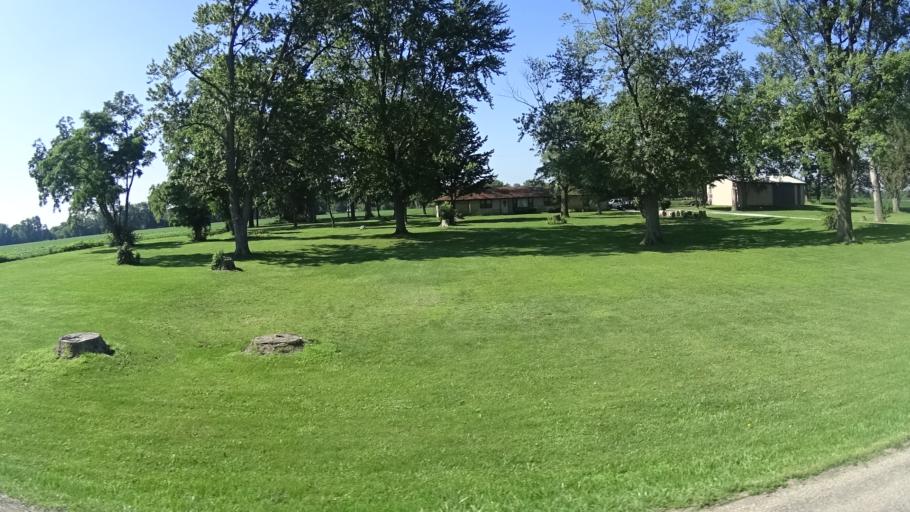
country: US
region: Indiana
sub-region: Madison County
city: Ingalls
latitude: 39.9879
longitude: -85.8105
